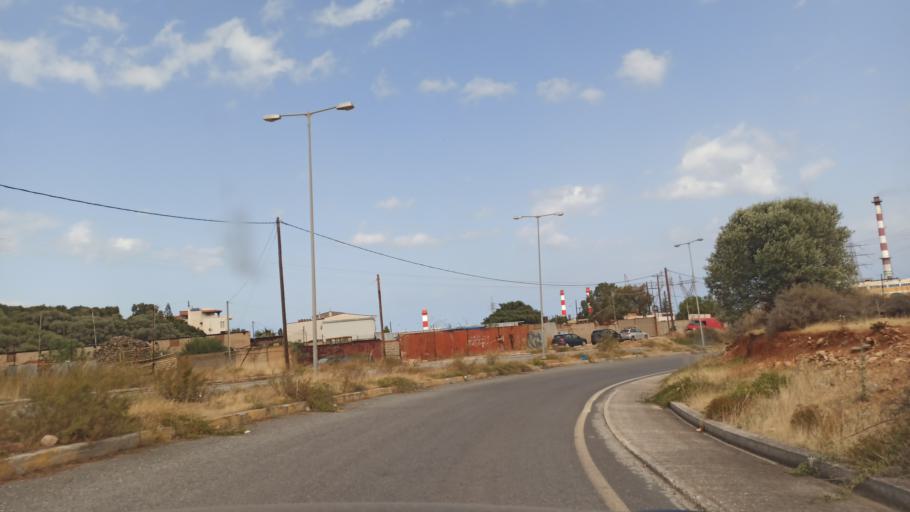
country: GR
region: Crete
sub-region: Nomos Irakleiou
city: Gazi
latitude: 35.3378
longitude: 25.0477
